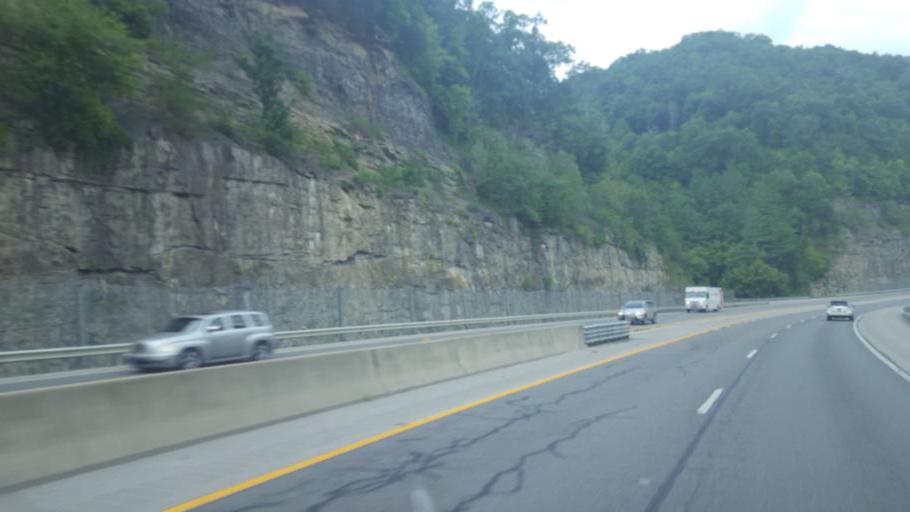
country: US
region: Kentucky
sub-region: Pike County
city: Pikeville
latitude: 37.4499
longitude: -82.5096
